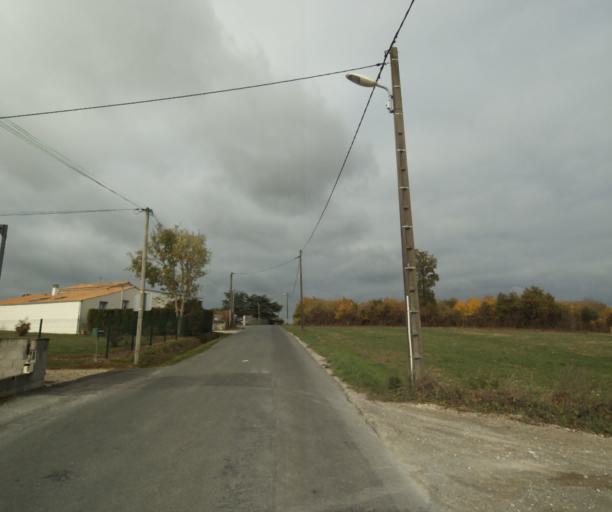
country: FR
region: Poitou-Charentes
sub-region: Departement de la Charente-Maritime
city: Saint-Georges-des-Coteaux
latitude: 45.7664
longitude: -0.6751
